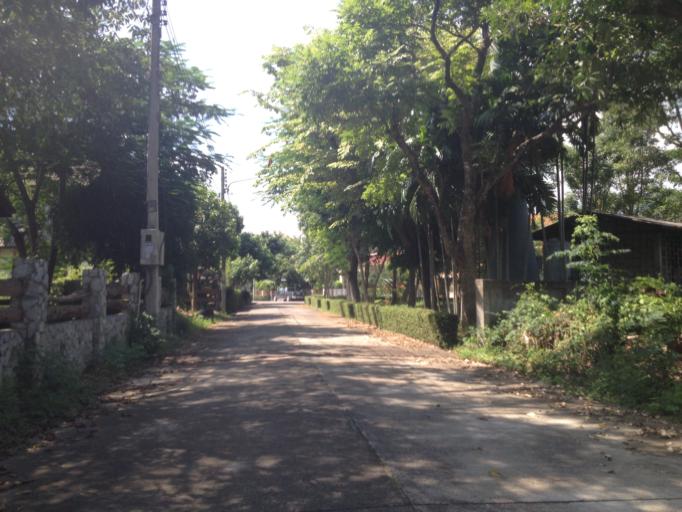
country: TH
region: Chiang Mai
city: Hang Dong
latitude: 18.7375
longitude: 98.9373
